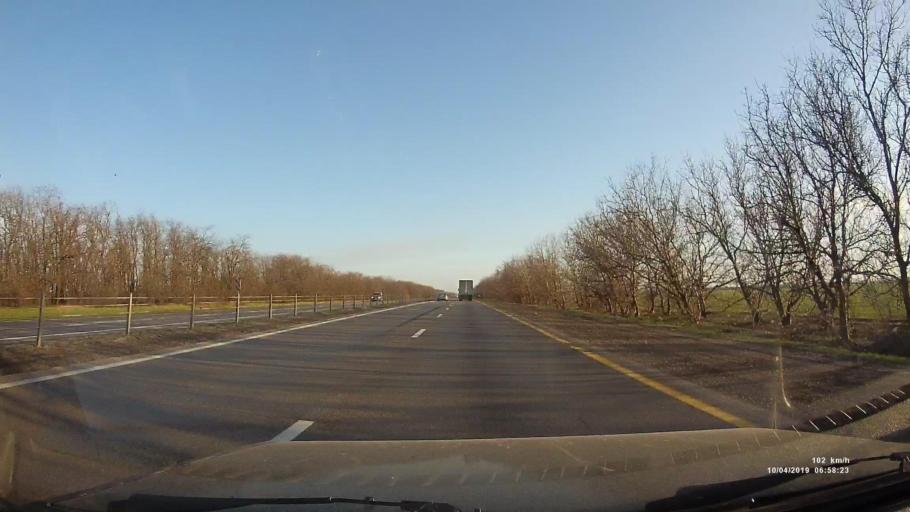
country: RU
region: Rostov
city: Grushevskaya
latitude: 47.5506
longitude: 39.9678
